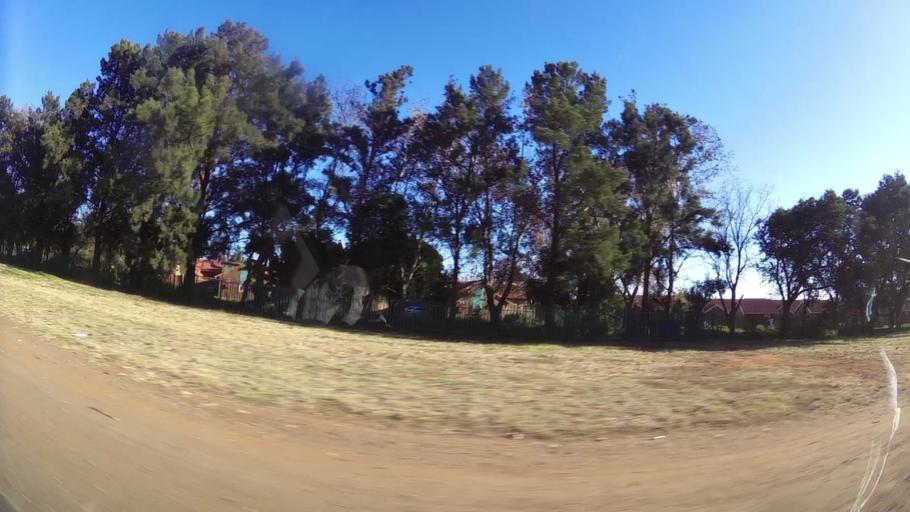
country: ZA
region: Gauteng
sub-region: Ekurhuleni Metropolitan Municipality
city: Tembisa
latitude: -26.0551
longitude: 28.2328
